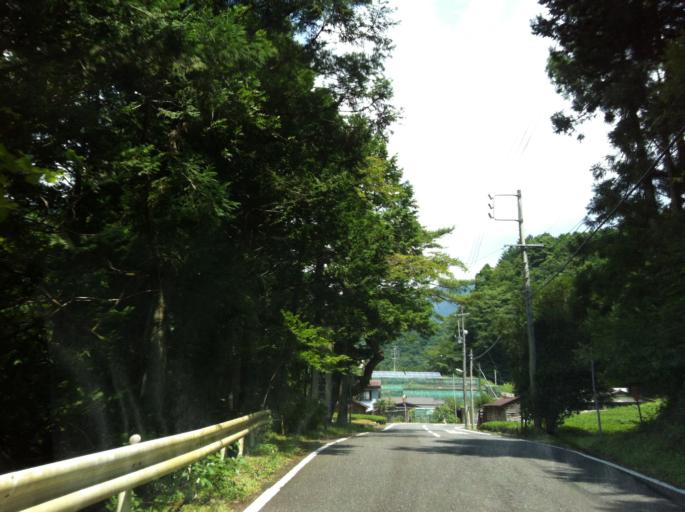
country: JP
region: Shizuoka
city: Shizuoka-shi
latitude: 35.2590
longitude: 138.3279
